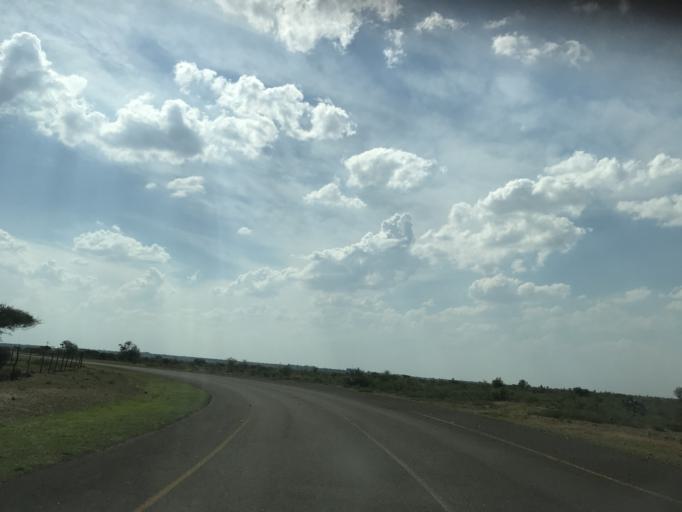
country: BW
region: South East
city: Janeng
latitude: -25.4938
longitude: 25.6393
